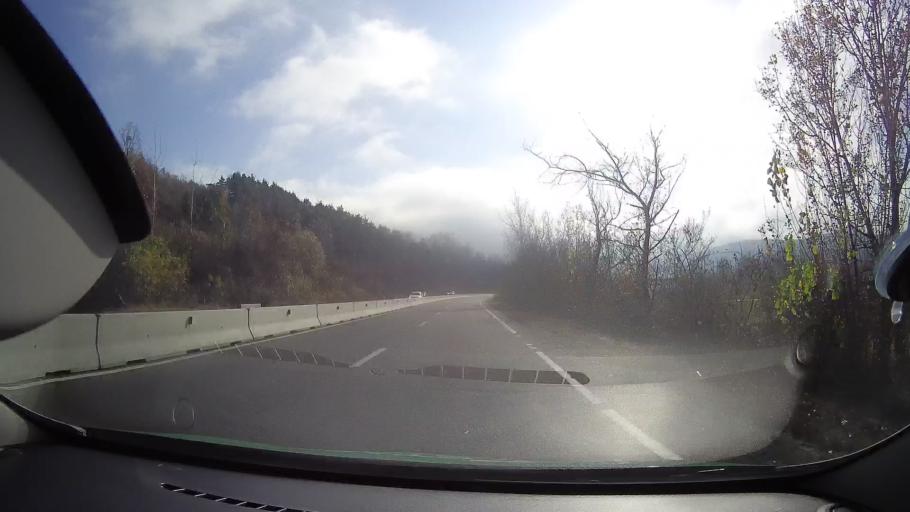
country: RO
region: Prahova
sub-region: Municipiul Campina
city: Campina
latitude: 45.1332
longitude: 25.7176
